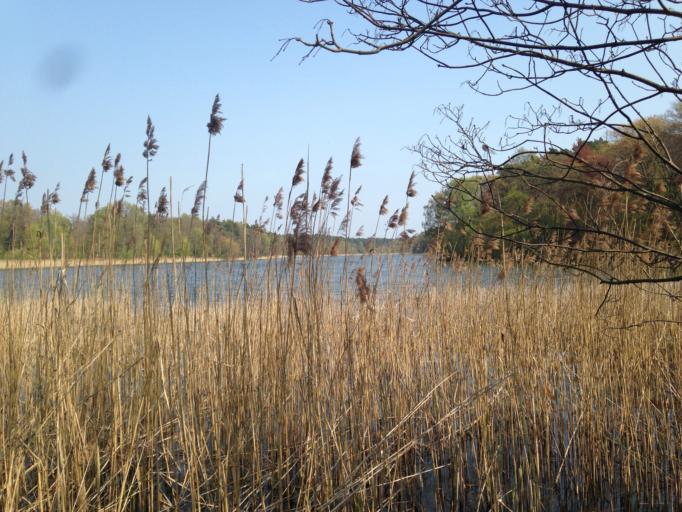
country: DE
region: Brandenburg
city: Kremmen
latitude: 52.8136
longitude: 13.0221
